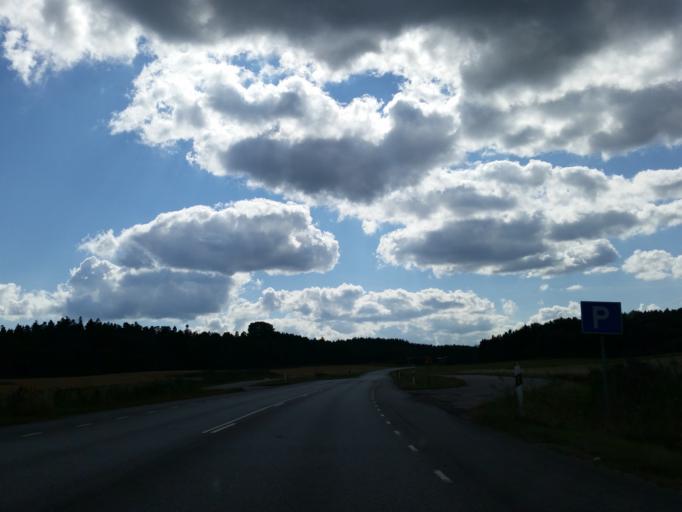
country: SE
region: Soedermanland
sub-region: Trosa Kommun
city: Vagnharad
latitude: 58.9501
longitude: 17.5455
